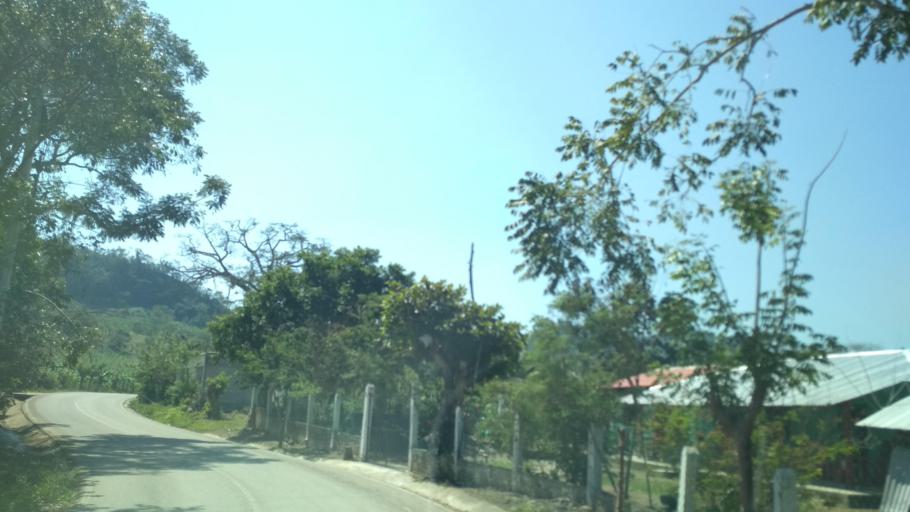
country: MX
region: Veracruz
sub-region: Papantla
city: Polutla
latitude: 20.4796
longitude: -97.2043
